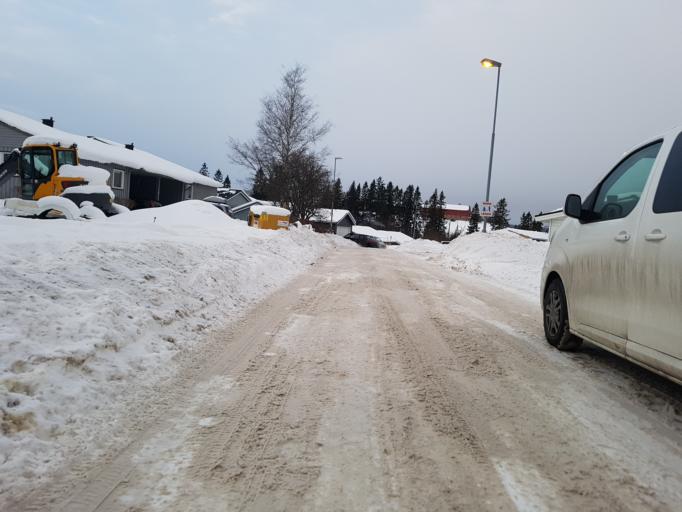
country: NO
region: Sor-Trondelag
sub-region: Trondheim
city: Trondheim
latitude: 63.3726
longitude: 10.3887
